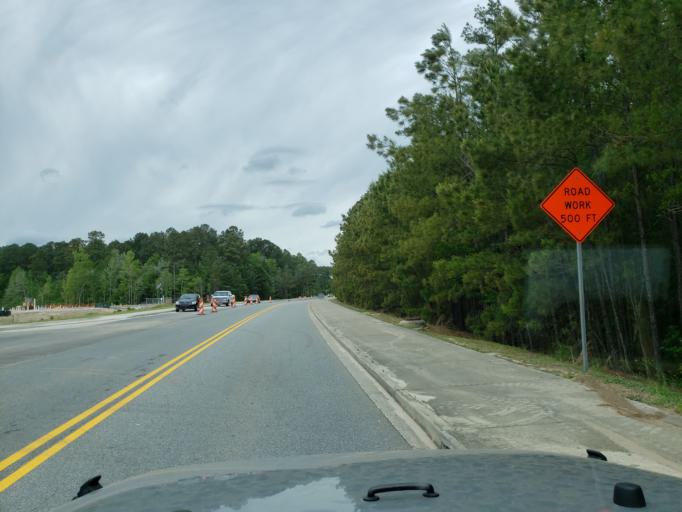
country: US
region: Georgia
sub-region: Chatham County
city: Pooler
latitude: 32.1718
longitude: -81.2243
